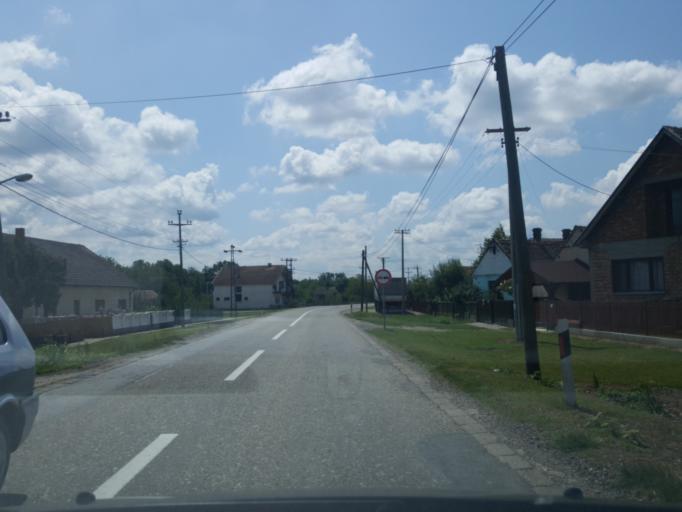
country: RS
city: Glusci
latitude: 44.8798
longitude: 19.5556
